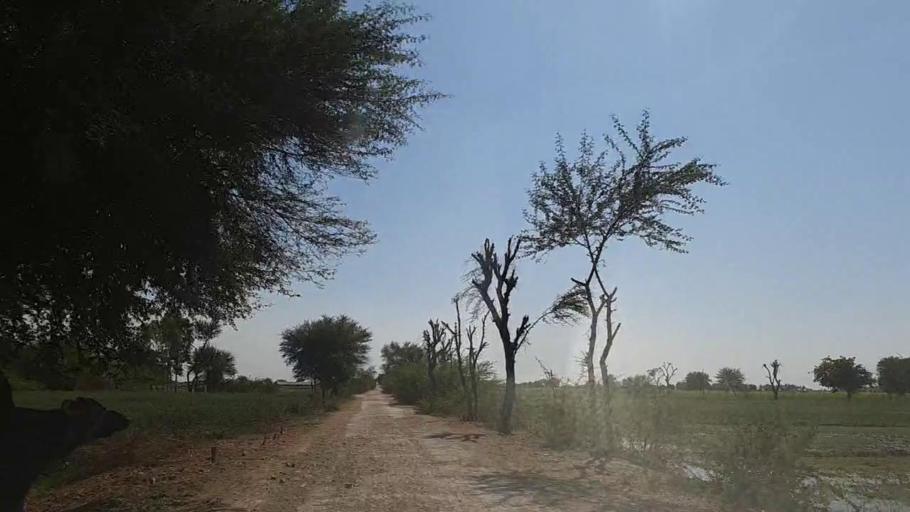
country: PK
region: Sindh
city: Kunri
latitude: 25.2801
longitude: 69.5226
